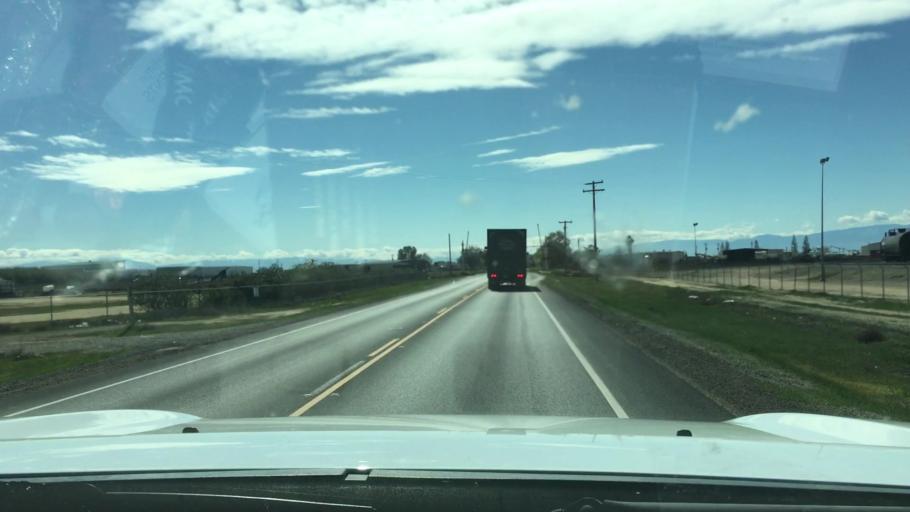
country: US
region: California
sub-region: Kern County
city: Shafter
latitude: 35.4519
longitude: -119.2571
